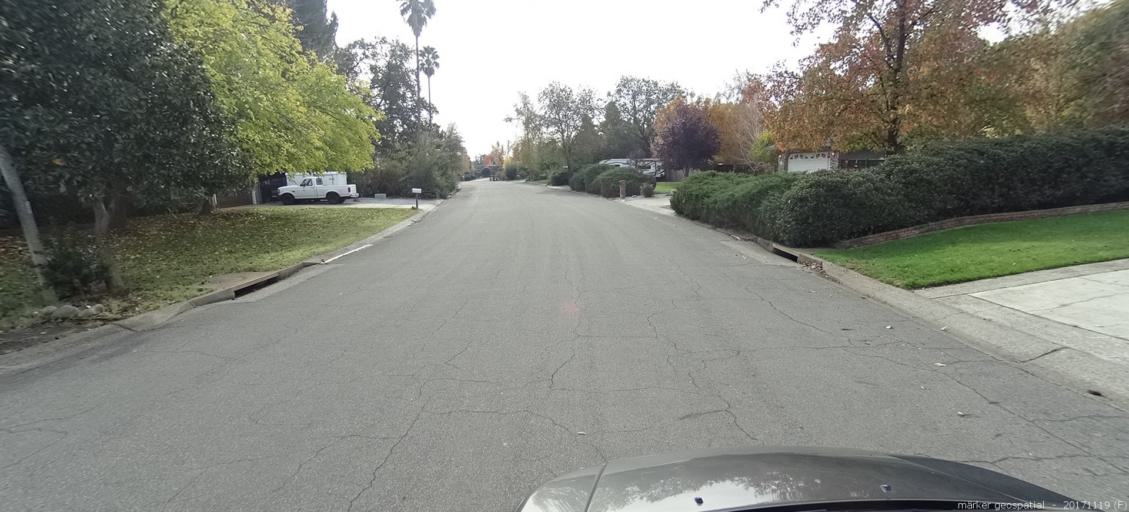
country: US
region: California
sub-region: Shasta County
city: Anderson
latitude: 40.4907
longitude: -122.3079
